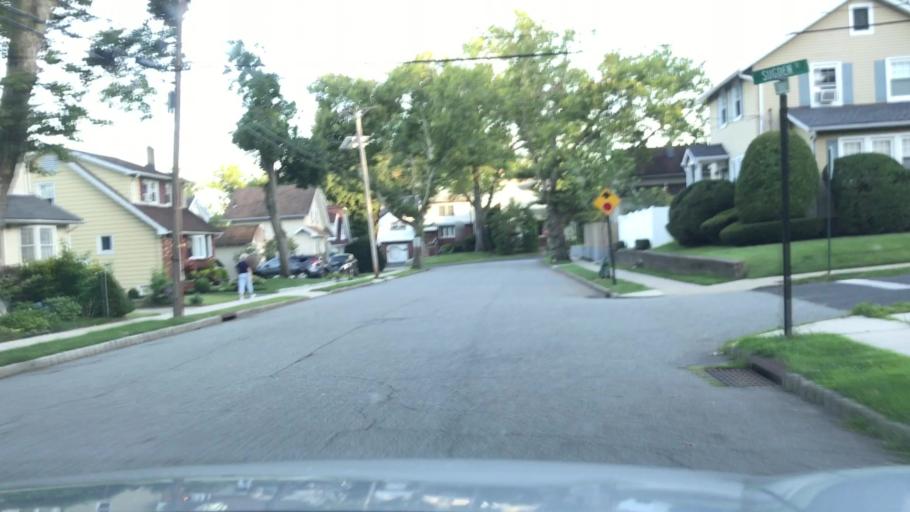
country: US
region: New Jersey
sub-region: Bergen County
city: Bergenfield
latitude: 40.9251
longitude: -74.0034
